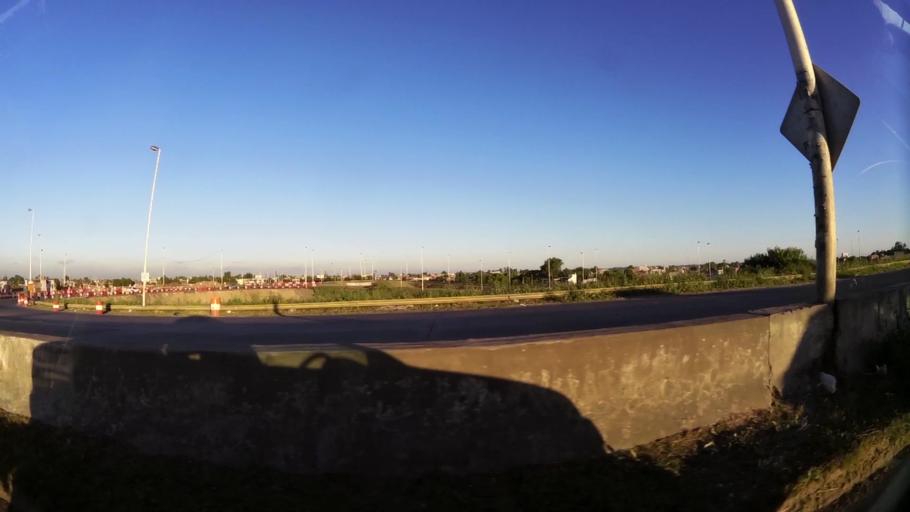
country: AR
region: Buenos Aires
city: Pontevedra
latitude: -34.7591
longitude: -58.6157
